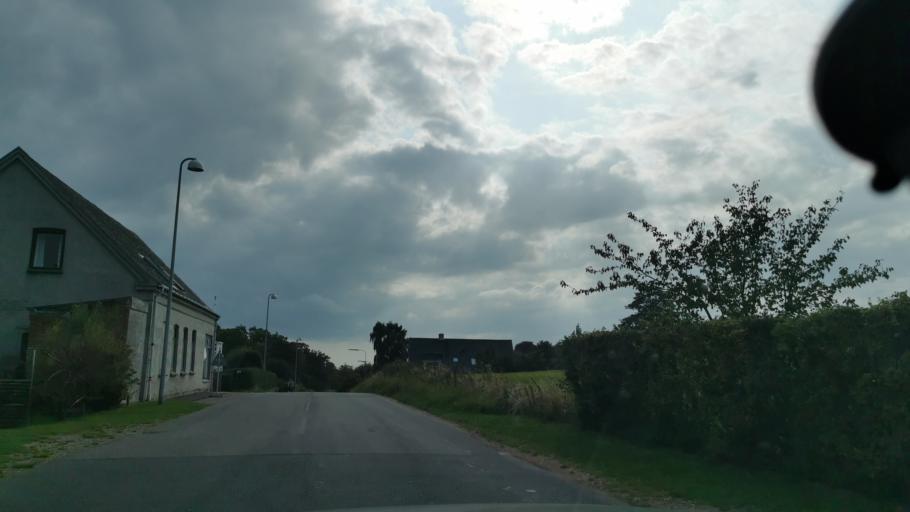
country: DK
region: Zealand
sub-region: Kalundborg Kommune
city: Kalundborg
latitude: 55.6965
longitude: 11.0660
